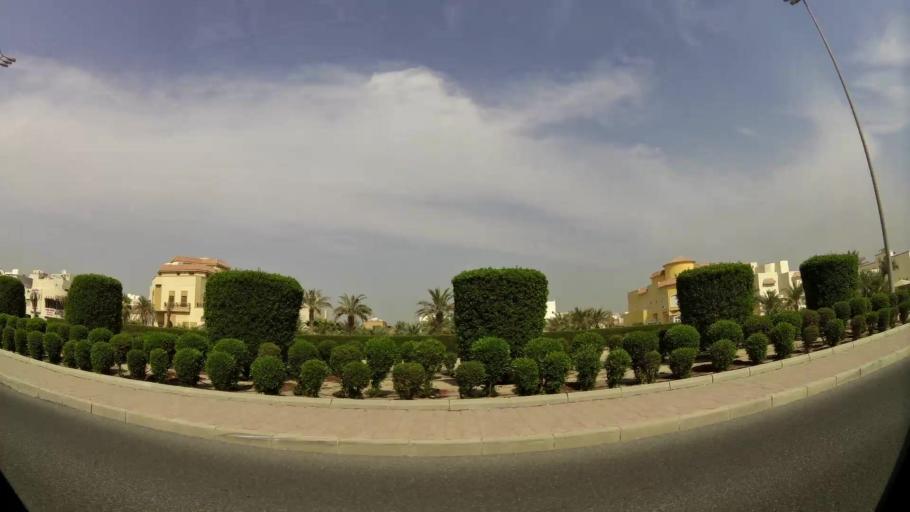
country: KW
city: Bayan
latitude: 29.2885
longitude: 48.0154
